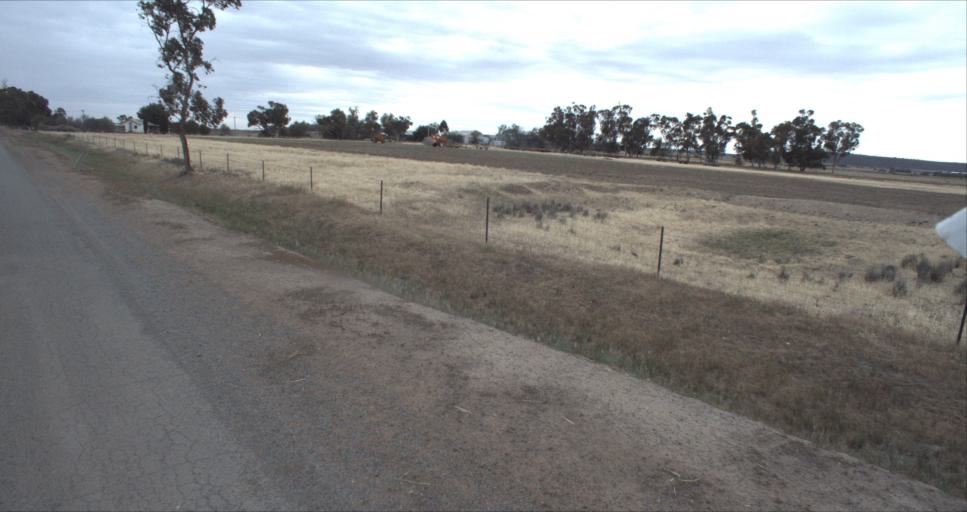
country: AU
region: New South Wales
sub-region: Leeton
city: Leeton
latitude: -34.4084
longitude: 146.3408
